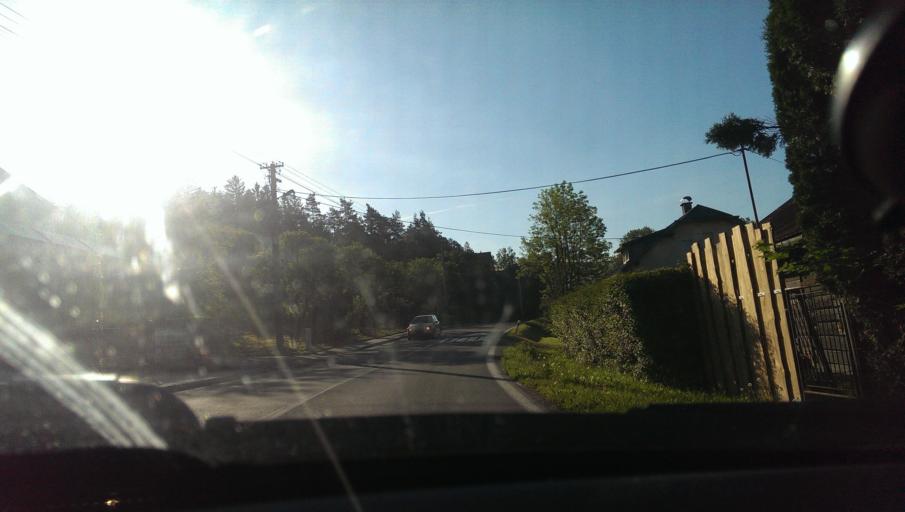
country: CZ
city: Kuncice pod Ondrejnikem
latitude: 49.5424
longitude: 18.2773
